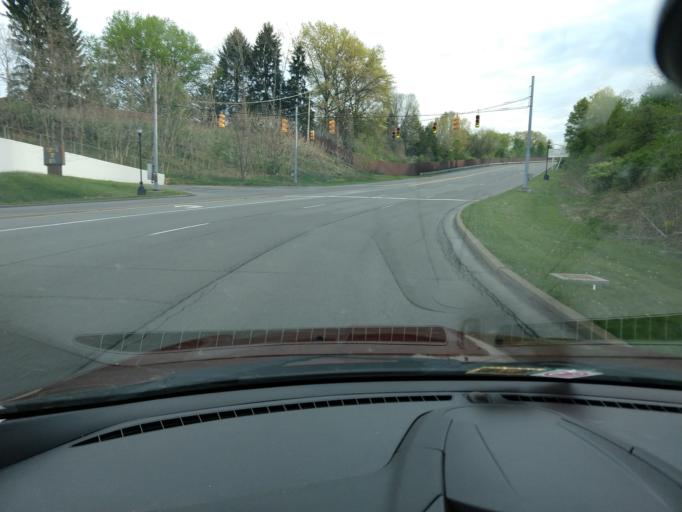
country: US
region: West Virginia
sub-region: Harrison County
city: Bridgeport
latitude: 39.3102
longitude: -80.2772
